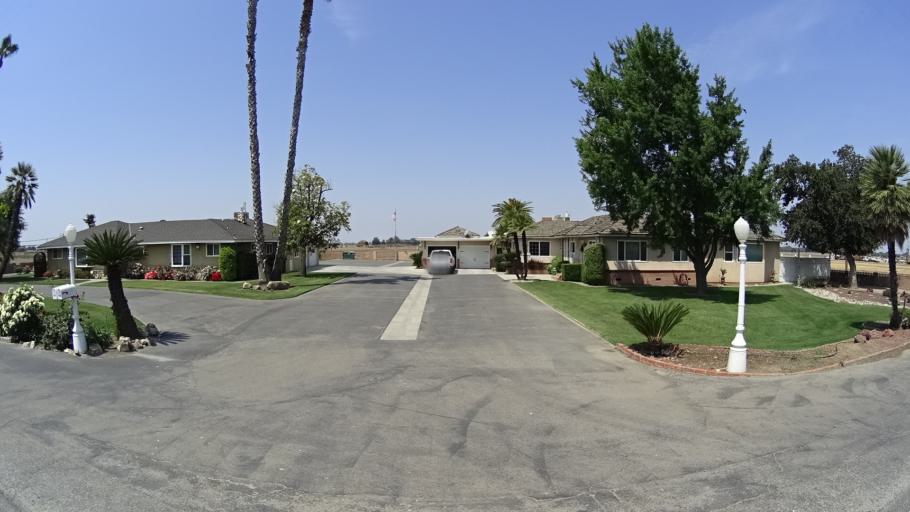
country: US
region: California
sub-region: Kings County
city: Lemoore
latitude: 36.3522
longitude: -119.7809
